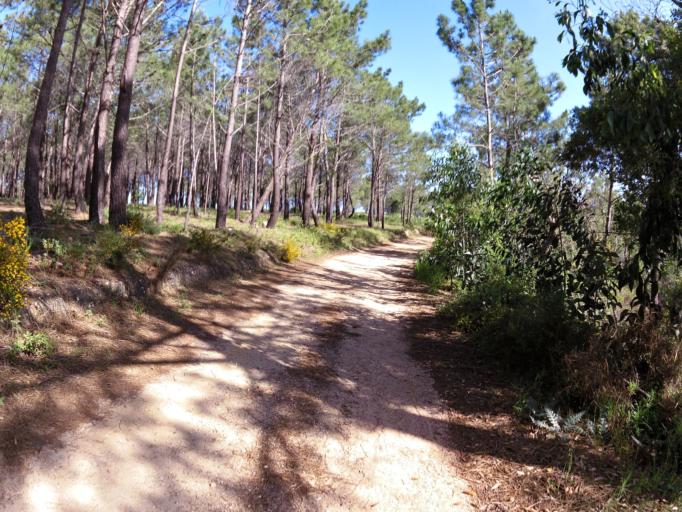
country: PT
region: Faro
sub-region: Aljezur
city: Aljezur
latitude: 37.3326
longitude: -8.8082
